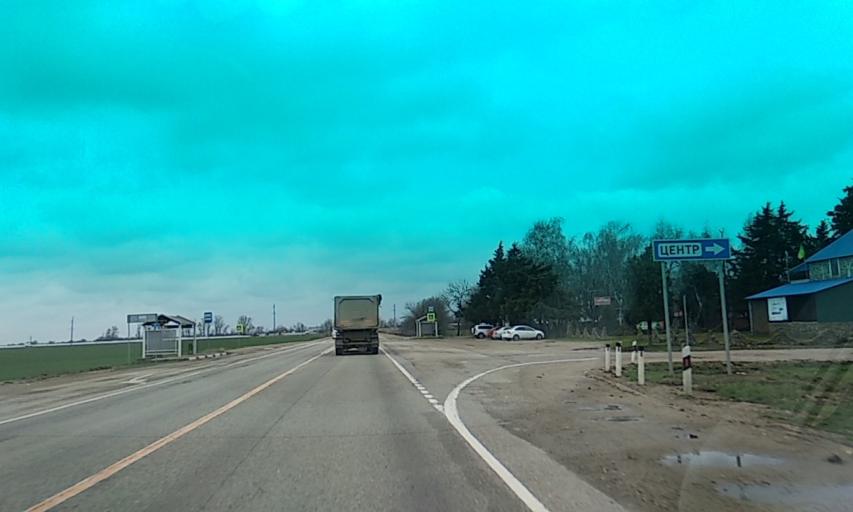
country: RU
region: Adygeya
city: Beloye
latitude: 45.0044
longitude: 39.7036
